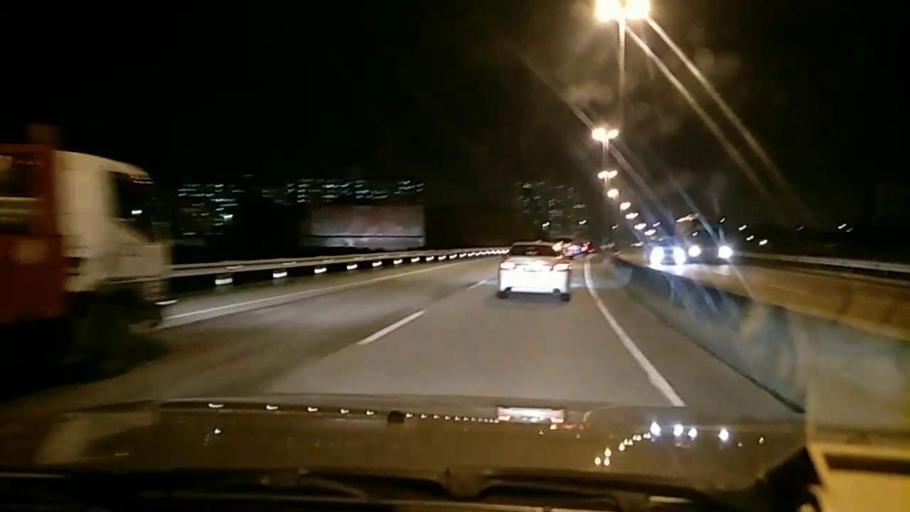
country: MY
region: Kuala Lumpur
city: Kuala Lumpur
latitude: 3.1178
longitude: 101.7165
